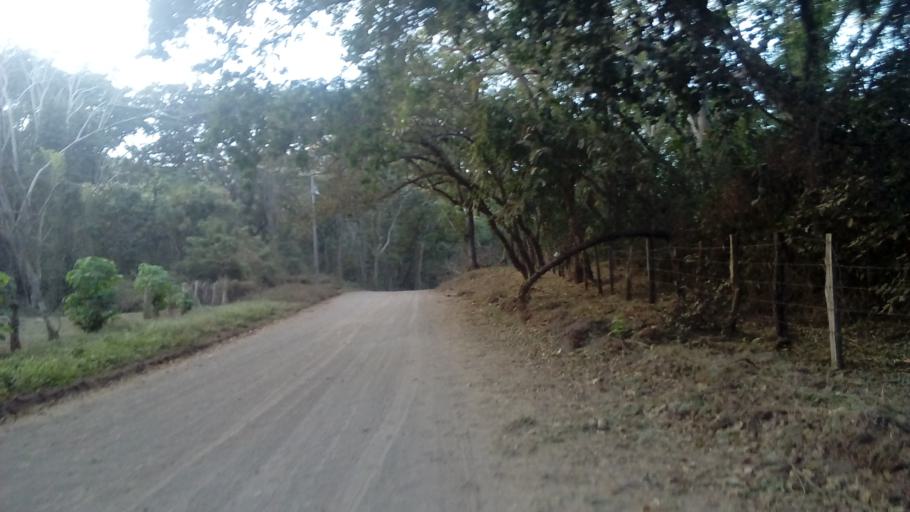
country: CR
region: Guanacaste
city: Sardinal
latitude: 10.3962
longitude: -85.8194
